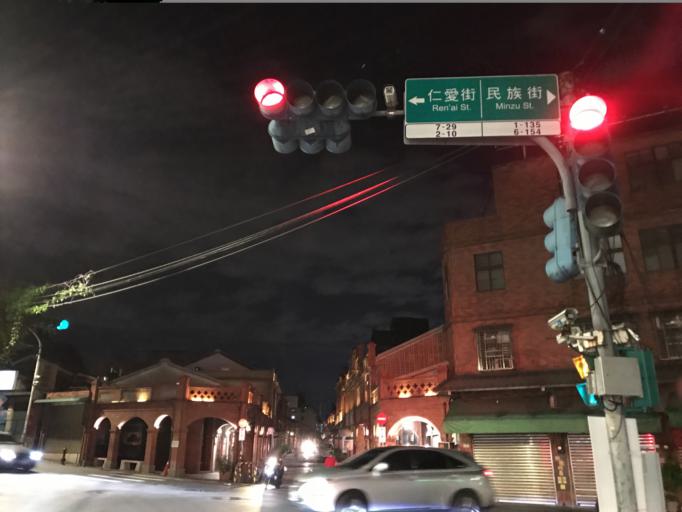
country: TW
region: Taiwan
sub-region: Taoyuan
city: Taoyuan
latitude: 24.9316
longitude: 121.3686
